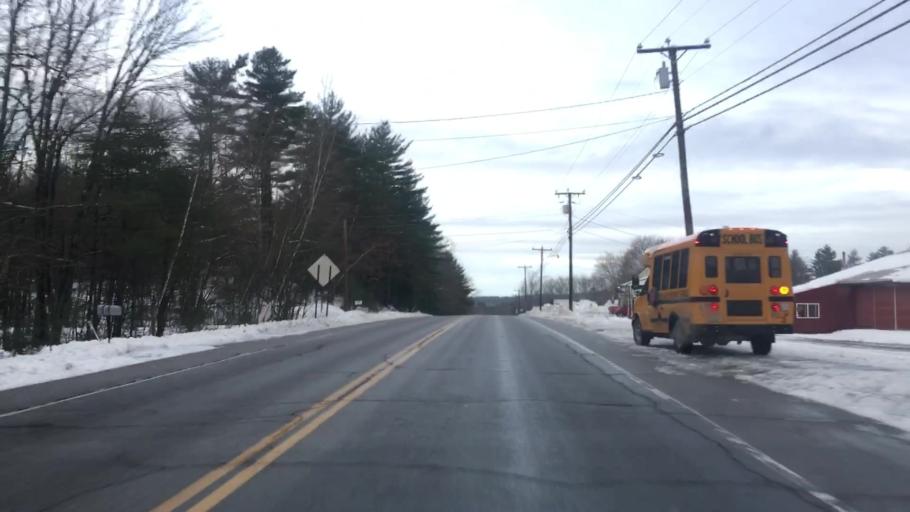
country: US
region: Maine
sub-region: Cumberland County
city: Steep Falls
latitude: 43.7375
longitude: -70.6343
